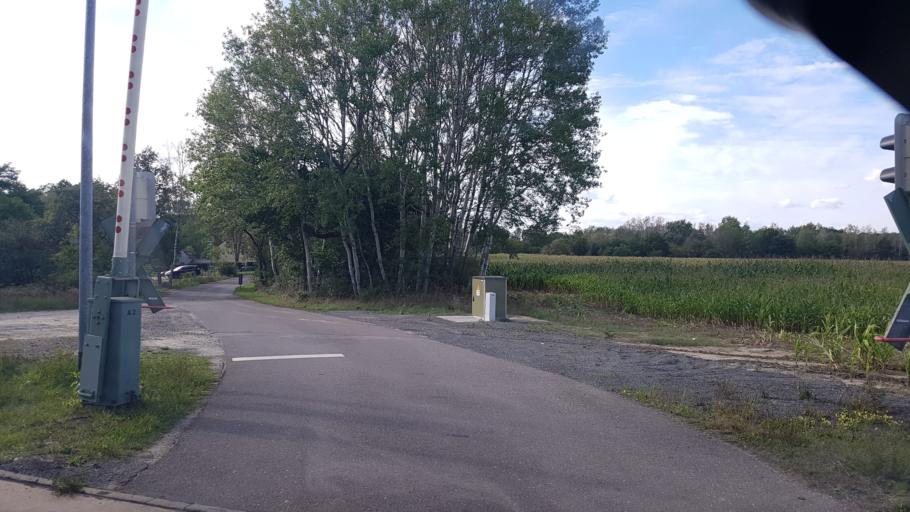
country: DE
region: Brandenburg
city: Spremberg
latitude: 51.5520
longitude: 14.3210
